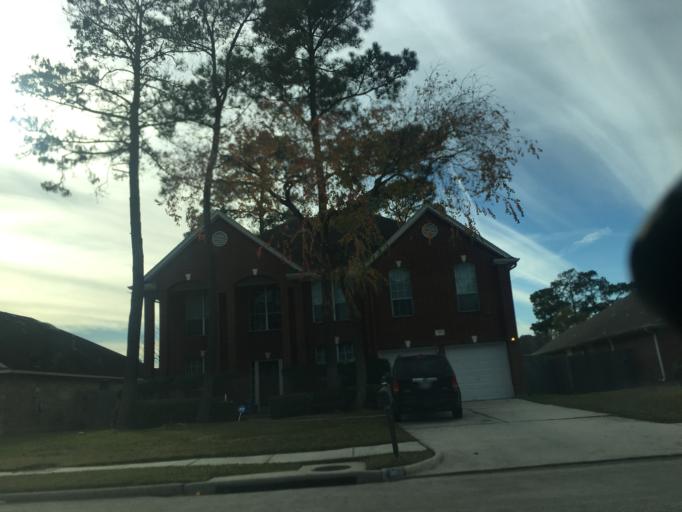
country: US
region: Texas
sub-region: Harris County
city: Cloverleaf
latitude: 29.8096
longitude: -95.1692
